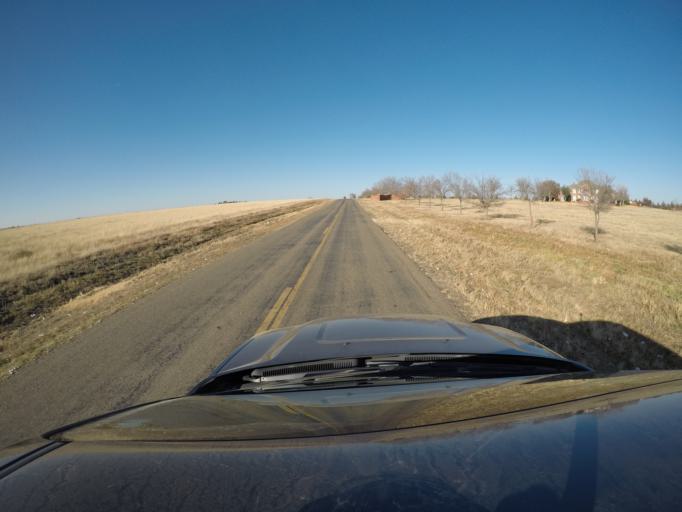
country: US
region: Texas
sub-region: Parmer County
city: Farwell
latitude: 34.3118
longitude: -103.0438
